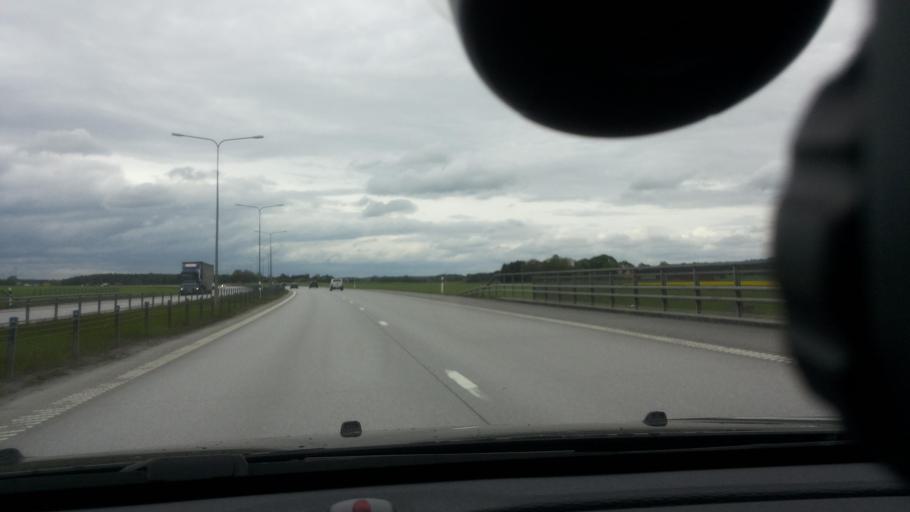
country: SE
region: Uppsala
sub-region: Uppsala Kommun
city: Saevja
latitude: 59.8531
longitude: 17.7329
